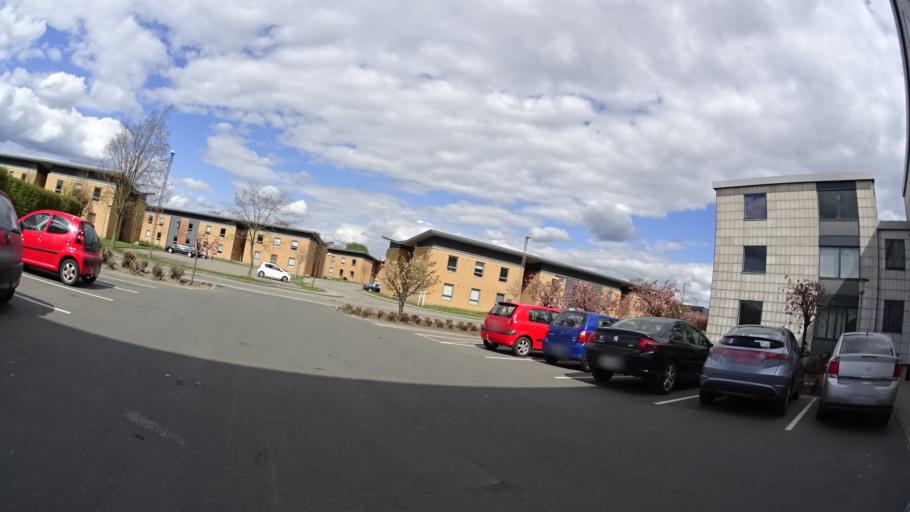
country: DK
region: Central Jutland
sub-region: Arhus Kommune
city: Stavtrup
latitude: 56.1319
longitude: 10.1557
